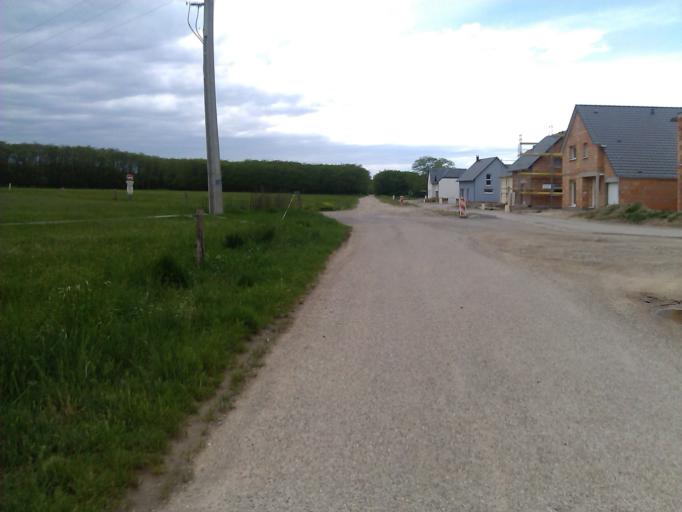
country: FR
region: Alsace
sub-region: Departement du Haut-Rhin
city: Ensisheim
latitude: 47.8548
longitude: 7.3398
